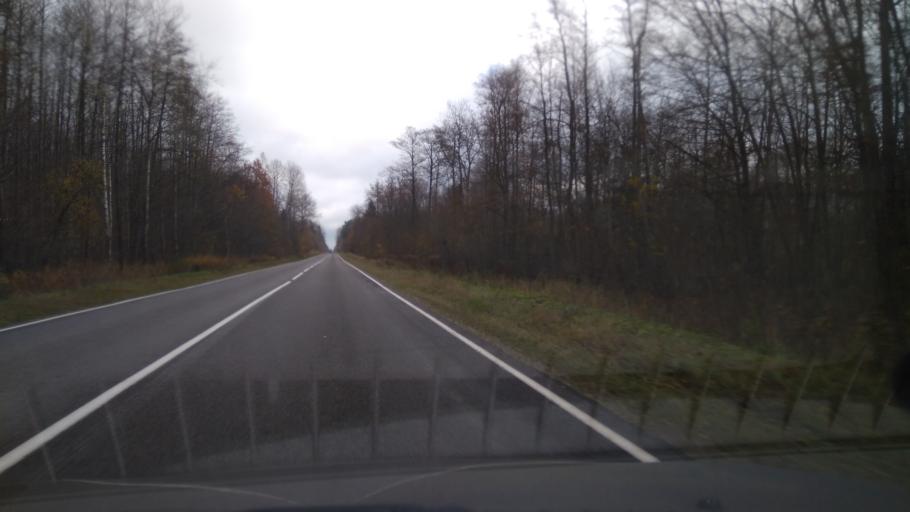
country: BY
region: Minsk
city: Urechcha
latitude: 53.2080
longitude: 27.9194
